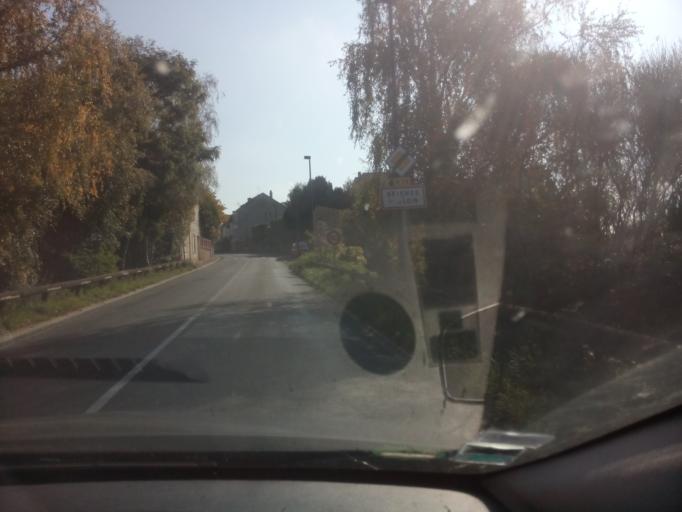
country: FR
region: Pays de la Loire
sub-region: Departement de Maine-et-Loire
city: Seiches-sur-le-Loir
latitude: 47.5763
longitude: -0.3648
